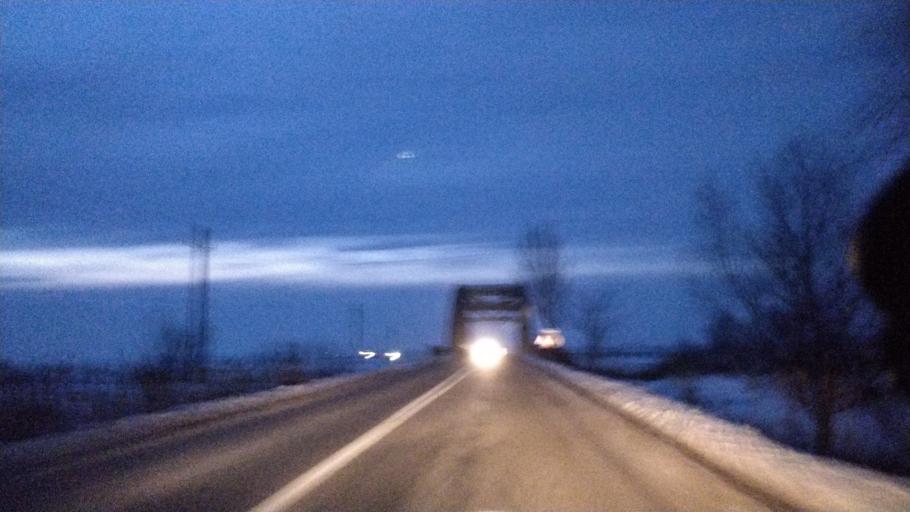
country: RO
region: Vrancea
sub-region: Comuna Rastoaca
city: Rastoaca
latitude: 45.6490
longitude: 27.3182
